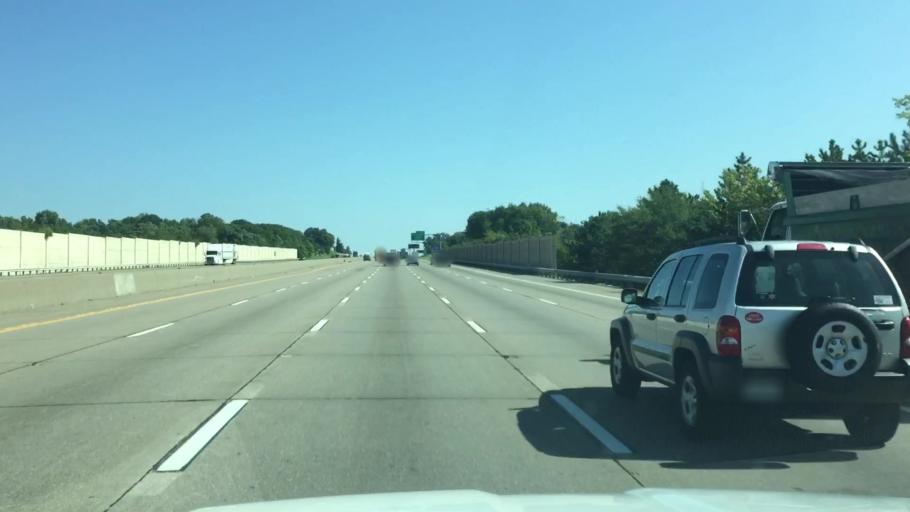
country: US
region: Missouri
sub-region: Jefferson County
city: Arnold
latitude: 38.4753
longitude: -90.3639
